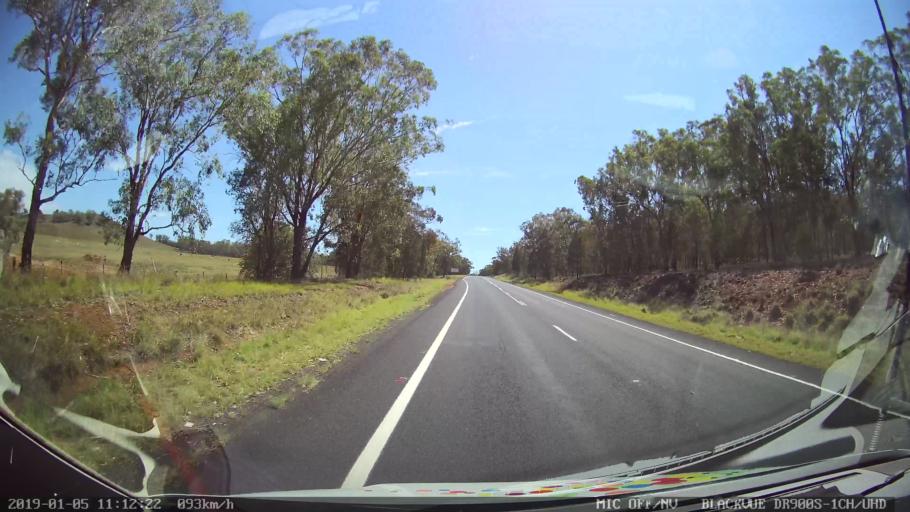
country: AU
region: New South Wales
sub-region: Warrumbungle Shire
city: Coonabarabran
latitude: -31.3828
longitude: 149.2599
